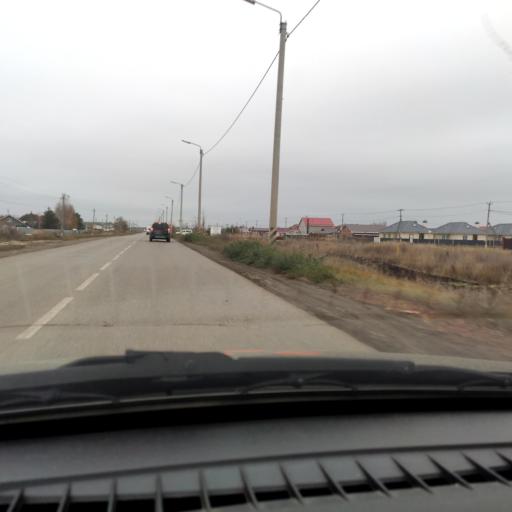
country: RU
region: Samara
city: Podstepki
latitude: 53.5226
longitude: 49.1605
